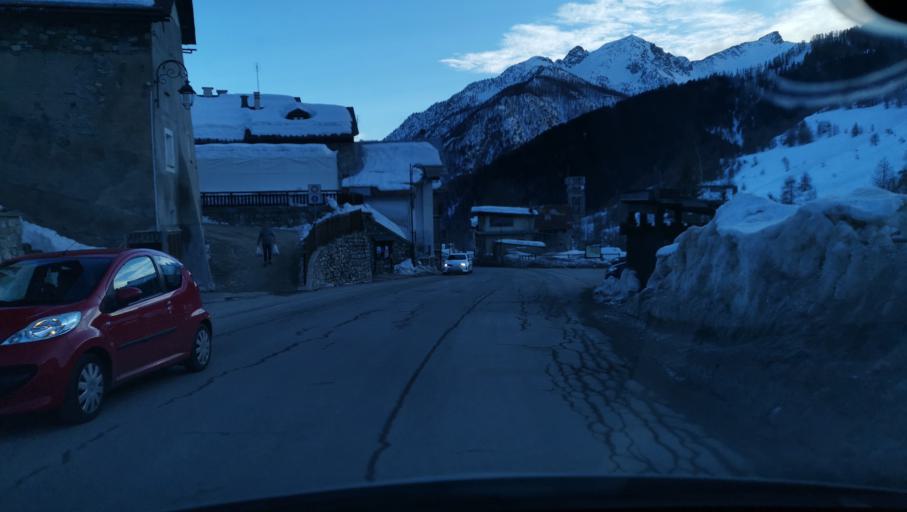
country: IT
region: Piedmont
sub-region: Provincia di Cuneo
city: Bersezio
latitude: 44.3797
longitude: 6.9688
